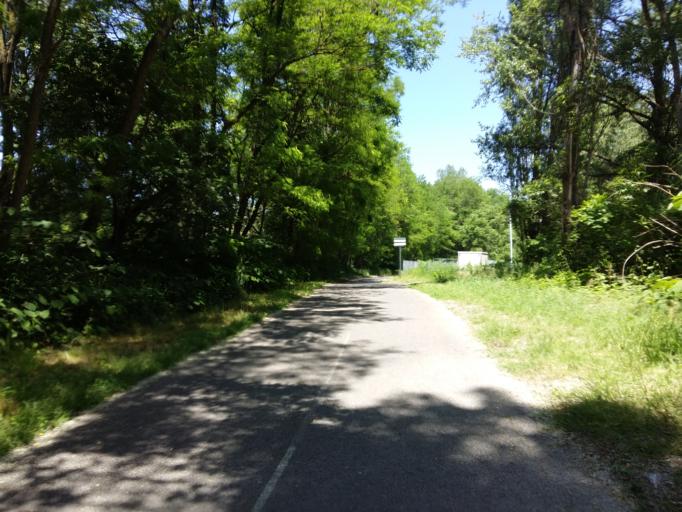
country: FR
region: Rhone-Alpes
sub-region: Departement du Rhone
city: Vaulx-en-Velin
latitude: 45.7901
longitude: 4.9019
